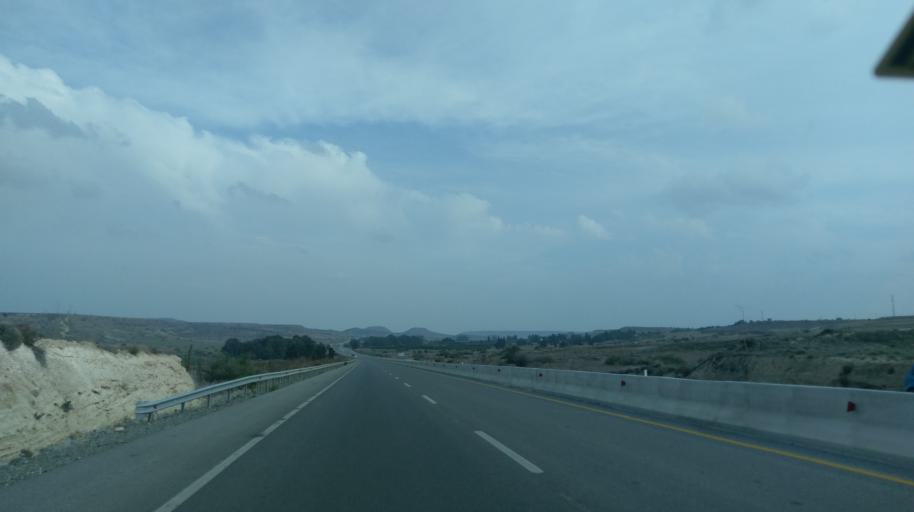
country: CY
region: Lefkosia
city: Astromeritis
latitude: 35.1957
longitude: 33.0743
